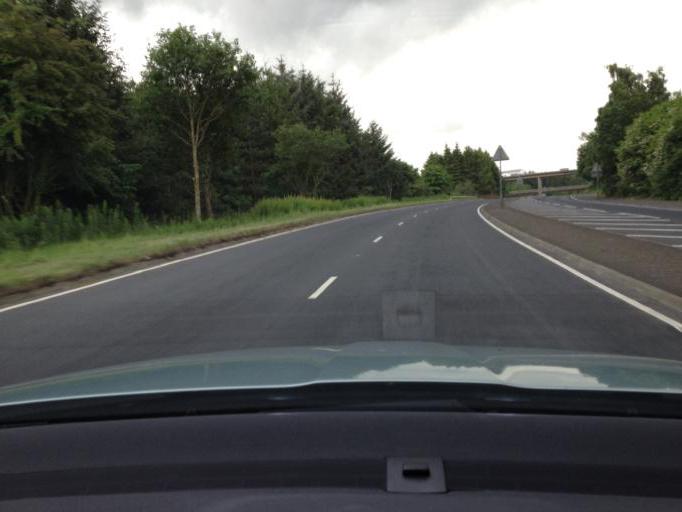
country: GB
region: Scotland
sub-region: Perth and Kinross
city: Perth
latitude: 56.3719
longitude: -3.4232
